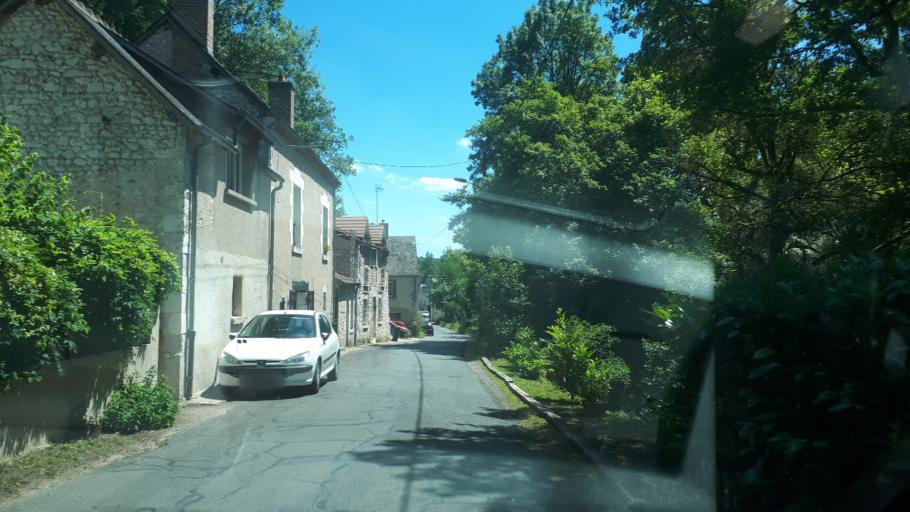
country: FR
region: Centre
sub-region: Departement du Loir-et-Cher
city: Saint-Sulpice-de-Pommeray
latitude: 47.5798
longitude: 1.2149
